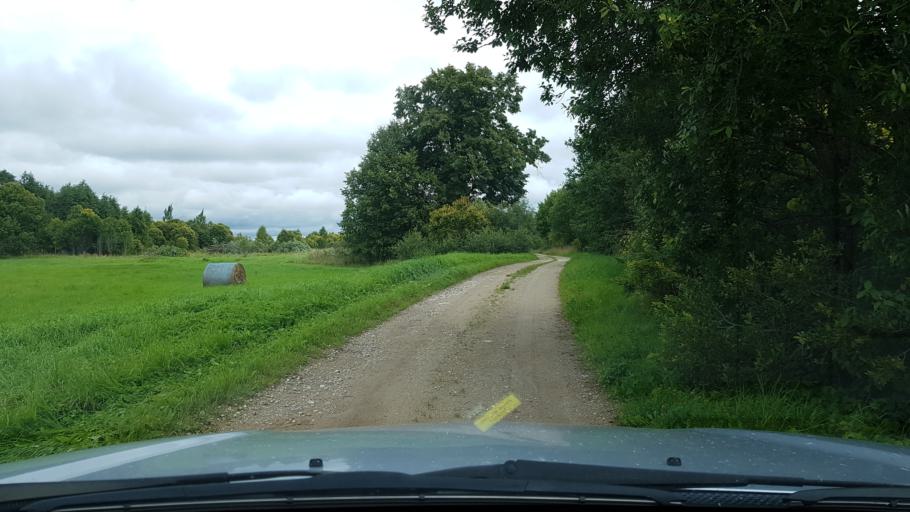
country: EE
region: Harju
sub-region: Rae vald
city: Vaida
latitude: 59.2753
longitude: 24.9640
